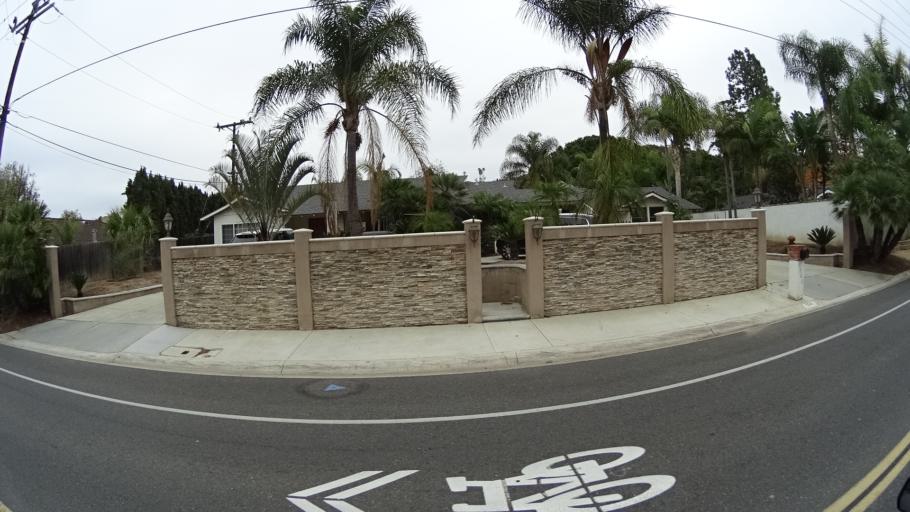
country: US
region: California
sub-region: Orange County
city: North Tustin
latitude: 33.7479
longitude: -117.7953
